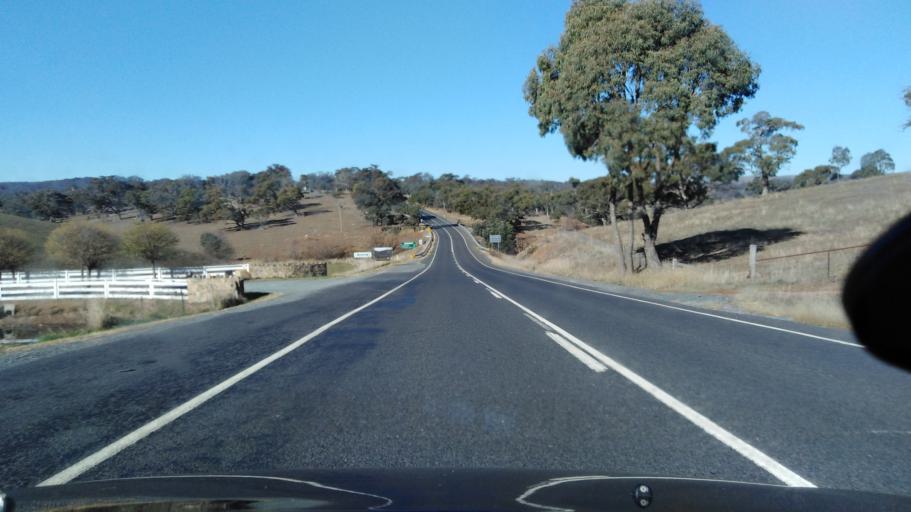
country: AU
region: New South Wales
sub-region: Yass Valley
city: Gundaroo
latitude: -35.1802
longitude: 149.2702
